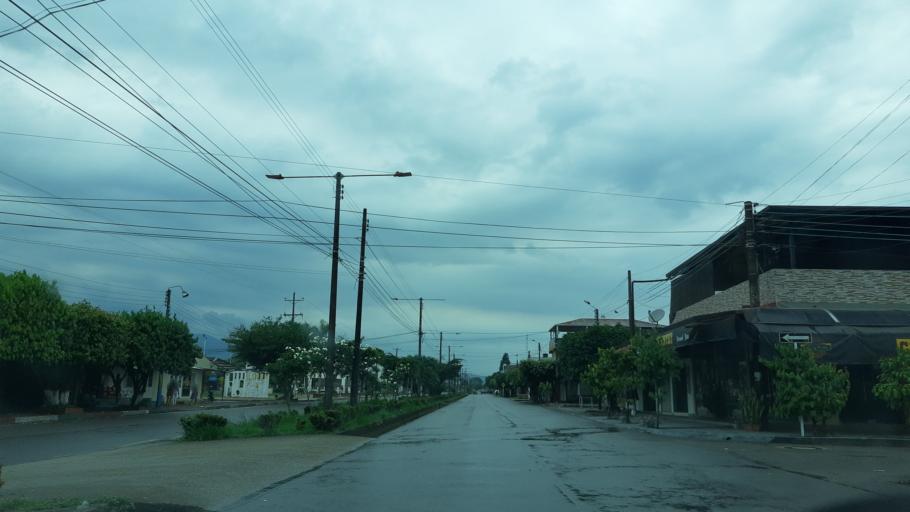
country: CO
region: Casanare
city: Monterrey
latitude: 4.8790
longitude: -72.8960
